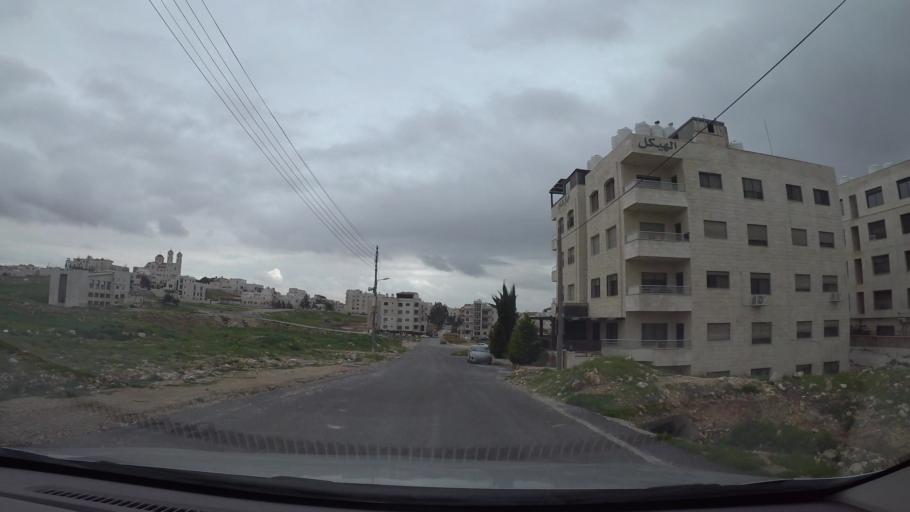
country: JO
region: Amman
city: Al Jubayhah
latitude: 31.9945
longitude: 35.8401
